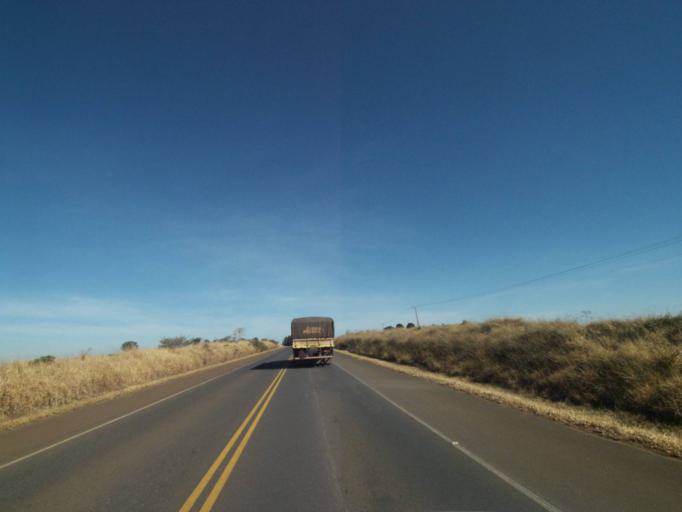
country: BR
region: Parana
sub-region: Tibagi
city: Tibagi
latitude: -24.3837
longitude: -50.3325
